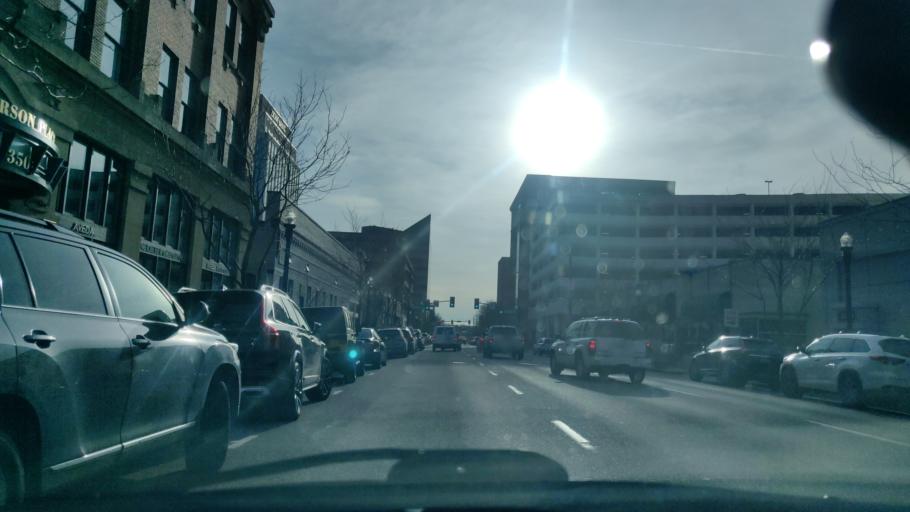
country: US
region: Idaho
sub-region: Ada County
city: Boise
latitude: 43.6184
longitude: -116.2026
